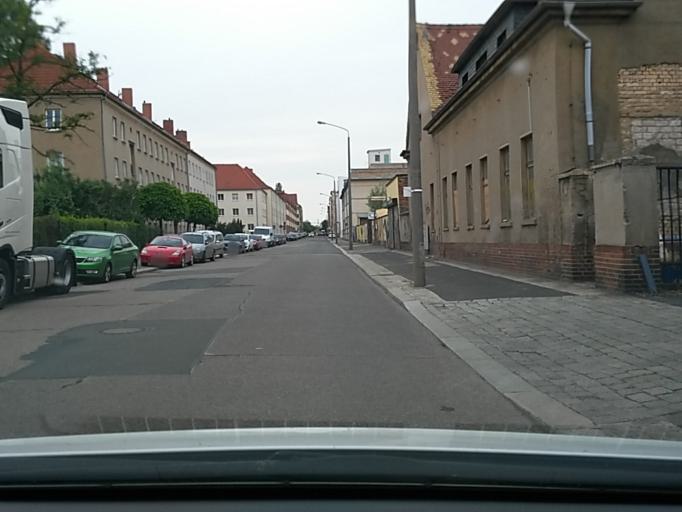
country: DE
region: Saxony-Anhalt
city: Halle (Saale)
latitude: 51.4837
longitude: 11.9991
